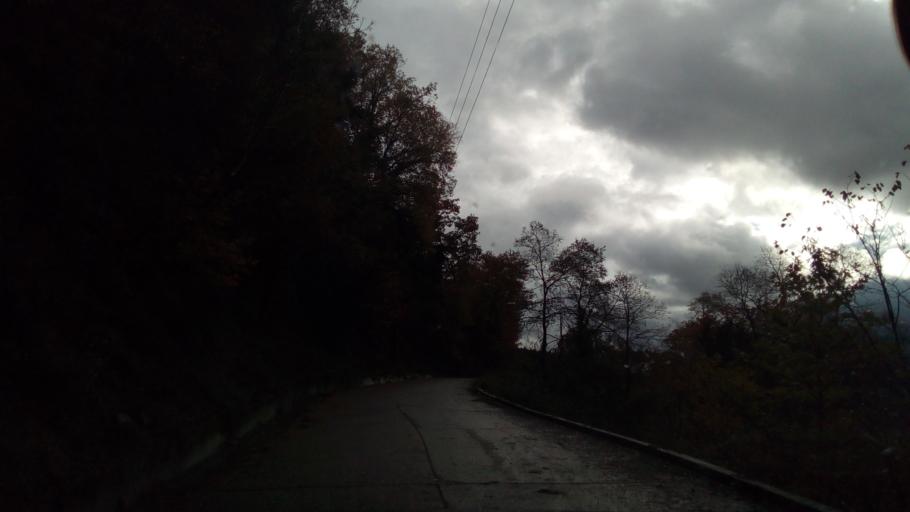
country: GR
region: West Greece
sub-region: Nomos Aitolias kai Akarnanias
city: Thermo
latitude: 38.6860
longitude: 21.8392
